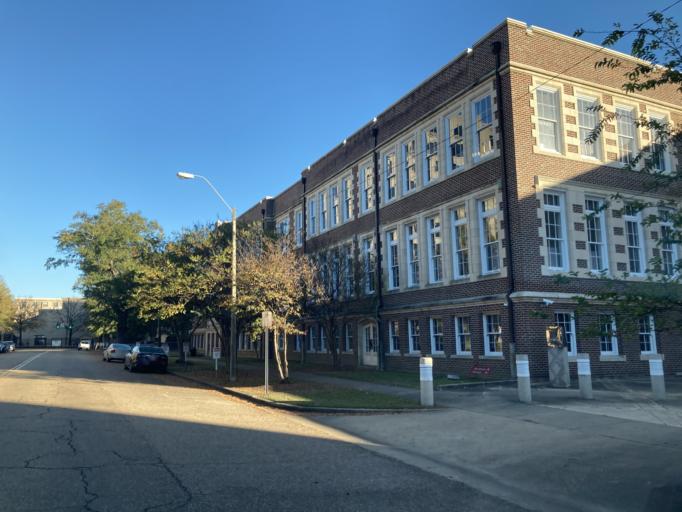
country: US
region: Mississippi
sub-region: Hinds County
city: Jackson
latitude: 32.3026
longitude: -90.1851
